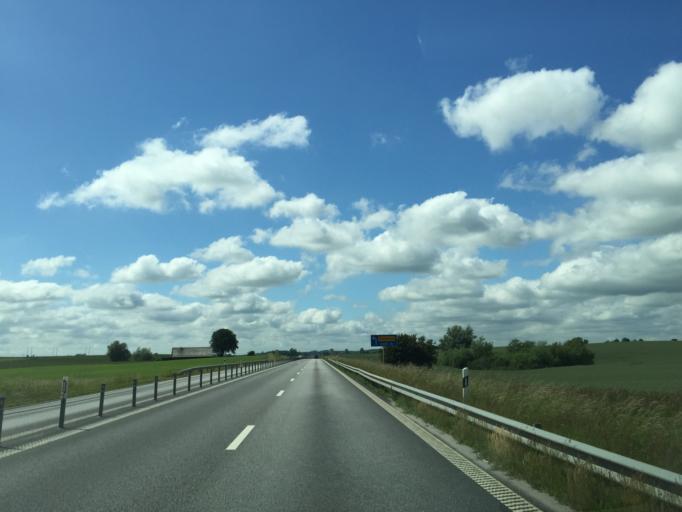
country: SE
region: Skane
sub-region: Skurups Kommun
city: Rydsgard
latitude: 55.4845
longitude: 13.5753
